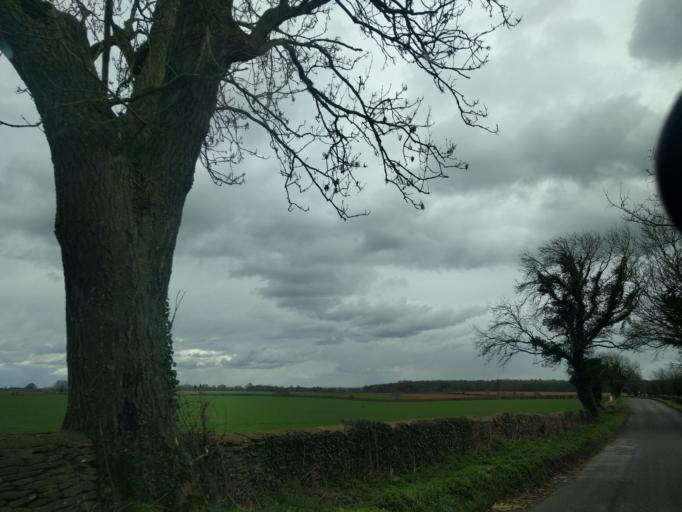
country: GB
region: England
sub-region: Gloucestershire
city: Nailsworth
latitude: 51.6294
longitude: -2.2281
